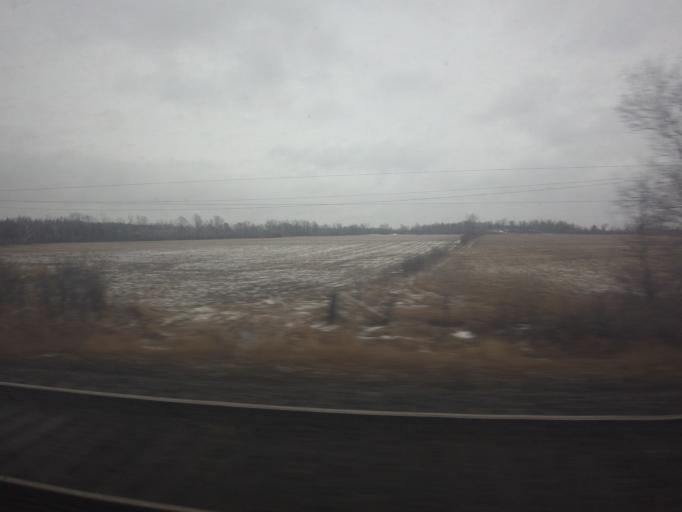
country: CA
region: Ontario
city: Gananoque
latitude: 44.3297
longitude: -76.3183
